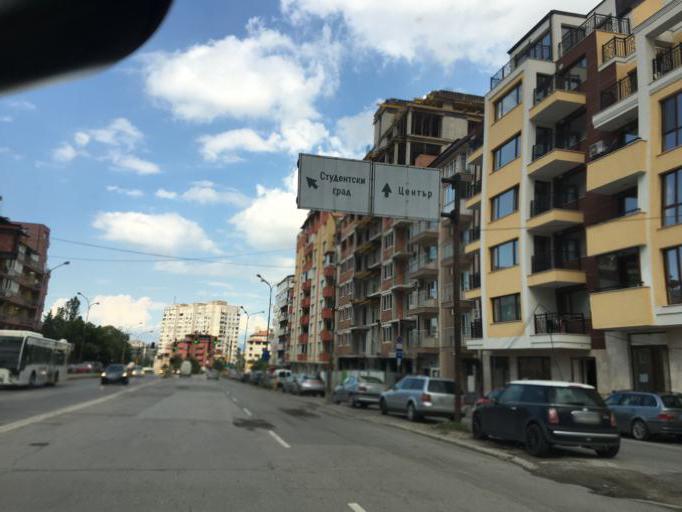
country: BG
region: Sofia-Capital
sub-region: Stolichna Obshtina
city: Sofia
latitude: 42.6501
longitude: 23.3578
